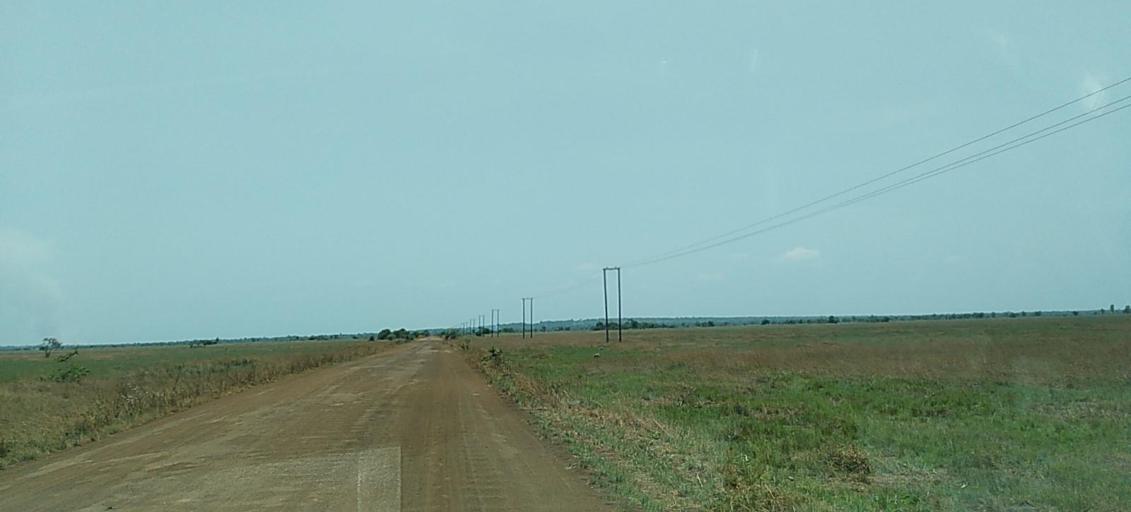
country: ZM
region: Copperbelt
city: Mpongwe
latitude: -13.6632
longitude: 27.8517
